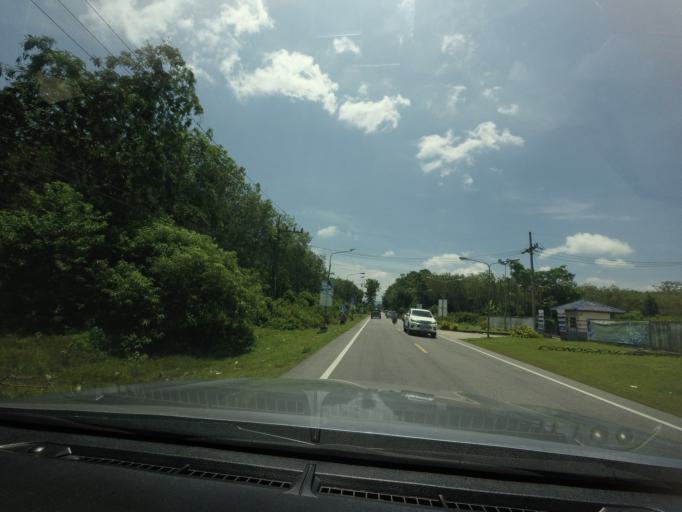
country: TH
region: Narathiwat
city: Rueso
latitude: 6.3621
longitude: 101.5013
